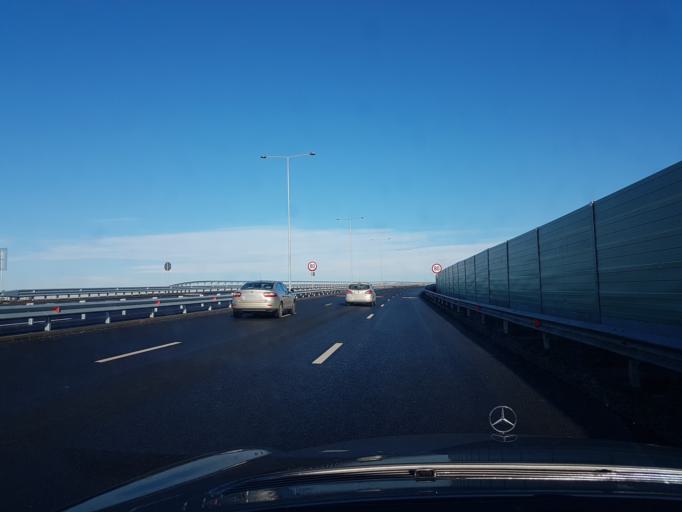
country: RO
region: Ilfov
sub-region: Comuna Fundeni-Dobroesti
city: Fundeni
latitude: 44.4806
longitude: 26.1381
